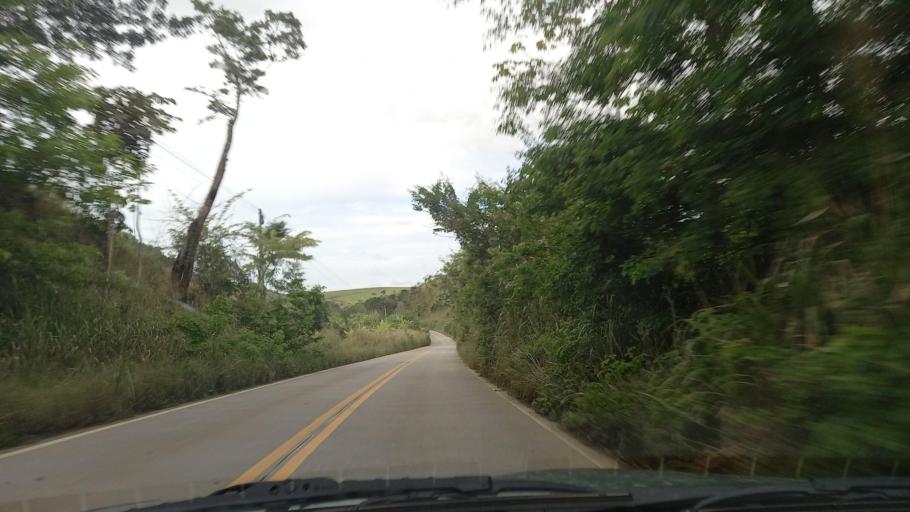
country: BR
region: Pernambuco
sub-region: Maraial
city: Maraial
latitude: -8.7623
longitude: -35.8593
